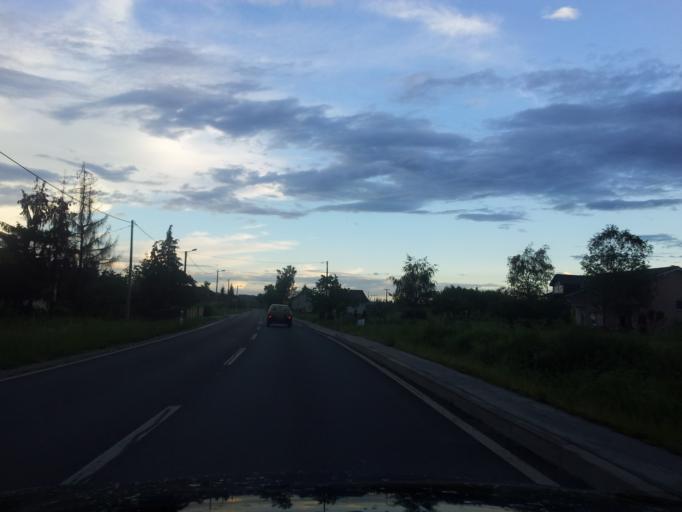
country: HR
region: Zagrebacka
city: Jastrebarsko
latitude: 45.6415
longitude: 15.6143
